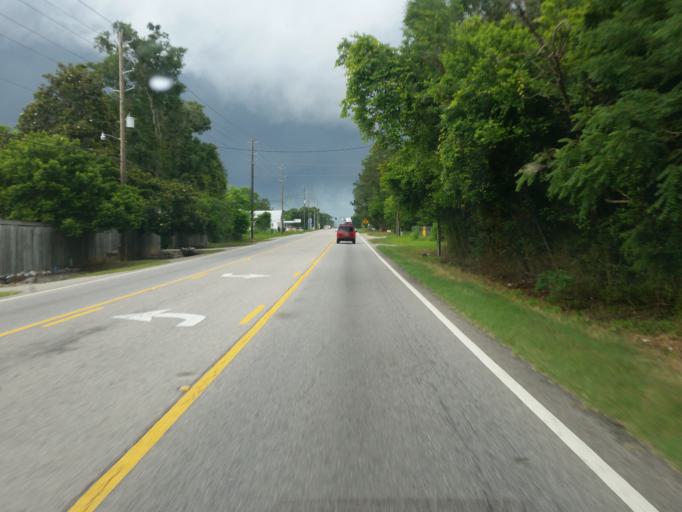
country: US
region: Mississippi
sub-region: Jackson County
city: Hurley
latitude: 30.7924
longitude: -88.3055
